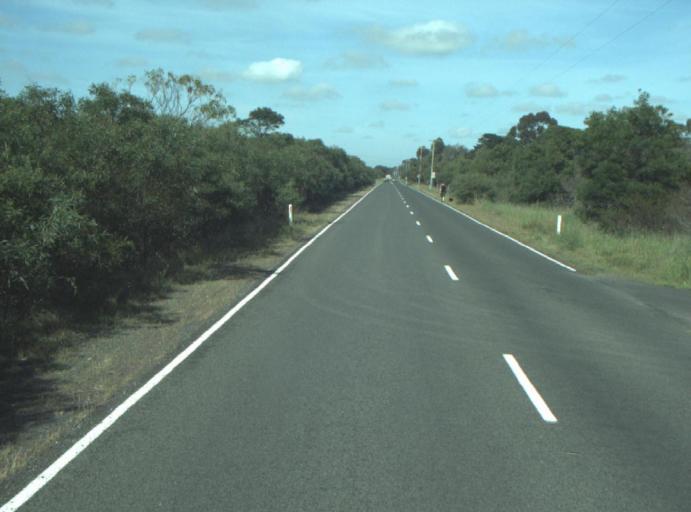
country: AU
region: Victoria
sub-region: Greater Geelong
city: Lara
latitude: -38.0090
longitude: 144.4301
